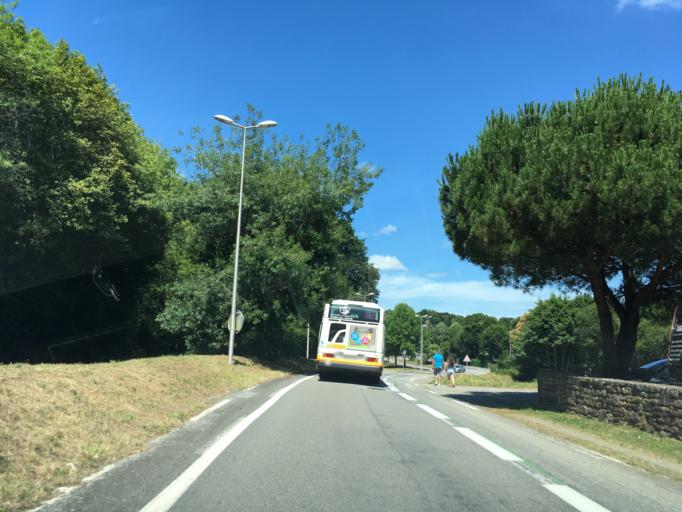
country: FR
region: Brittany
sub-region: Departement du Finistere
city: Quimper
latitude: 47.9745
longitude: -4.0834
